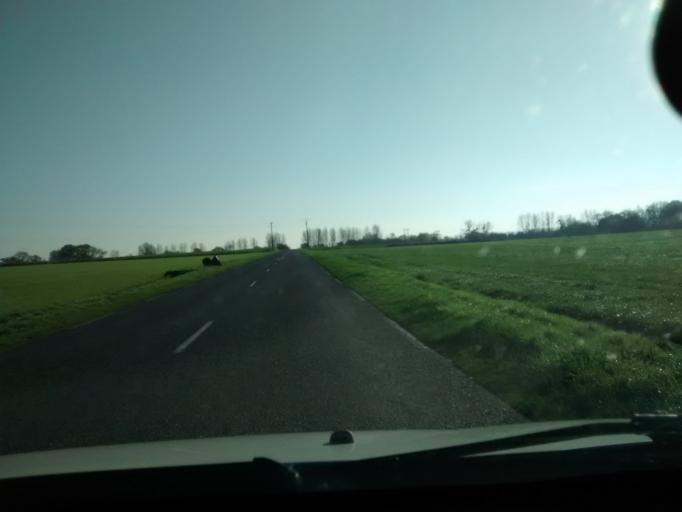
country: FR
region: Lower Normandy
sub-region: Departement de la Manche
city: Pontorson
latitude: 48.5318
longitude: -1.4874
